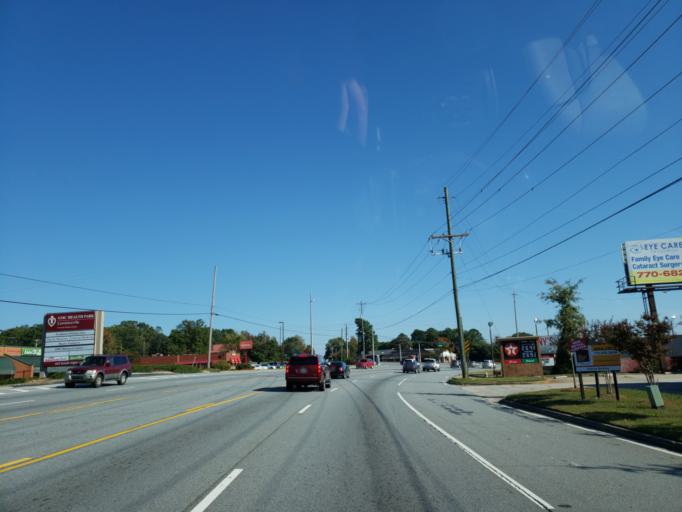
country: US
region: Georgia
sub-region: Gwinnett County
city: Lawrenceville
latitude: 33.9659
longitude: -84.0100
